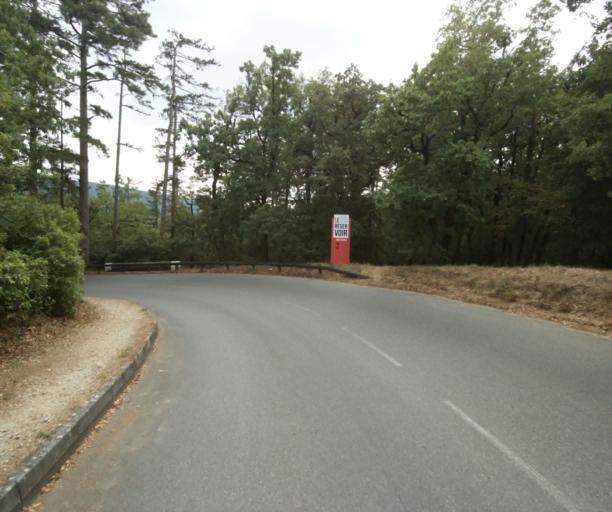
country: FR
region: Midi-Pyrenees
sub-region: Departement de la Haute-Garonne
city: Revel
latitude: 43.4378
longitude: 2.0188
